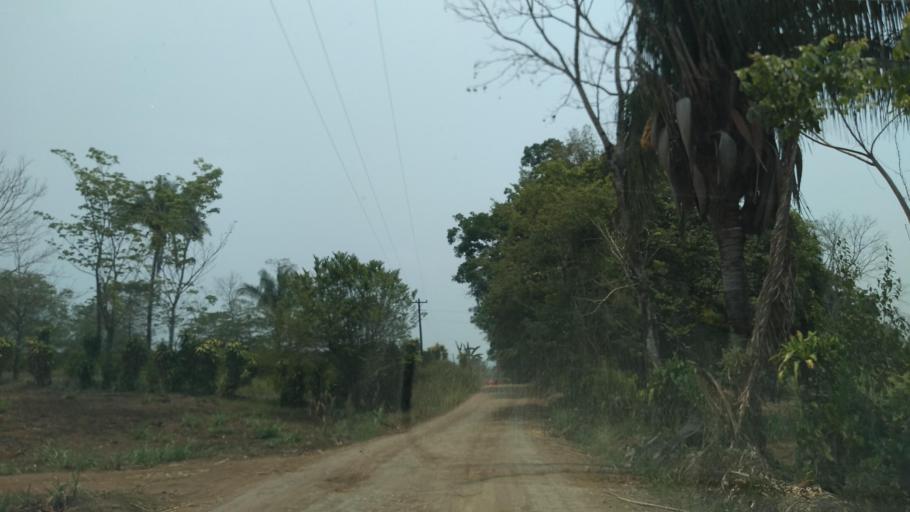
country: MX
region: Veracruz
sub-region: Tezonapa
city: Laguna Chica (Pueblo Nuevo)
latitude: 18.5029
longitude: -96.7727
